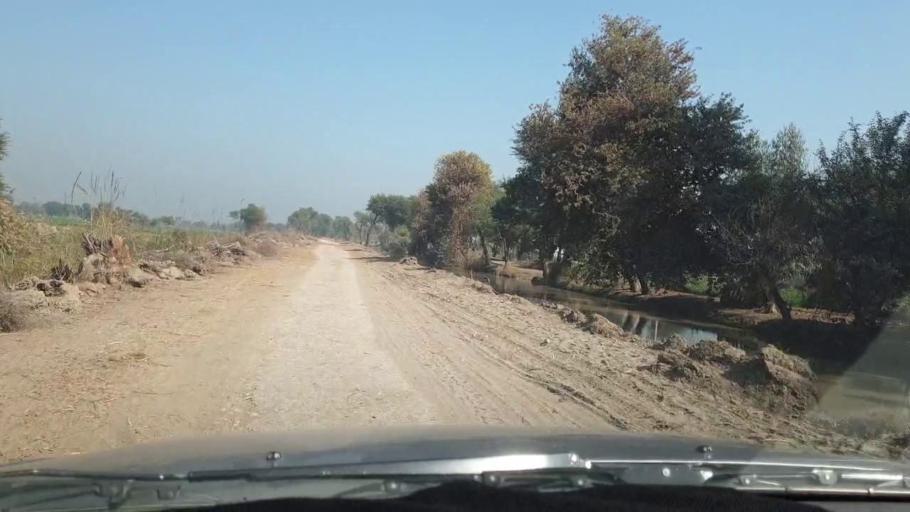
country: PK
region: Sindh
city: Khanpur
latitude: 27.7782
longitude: 69.5403
